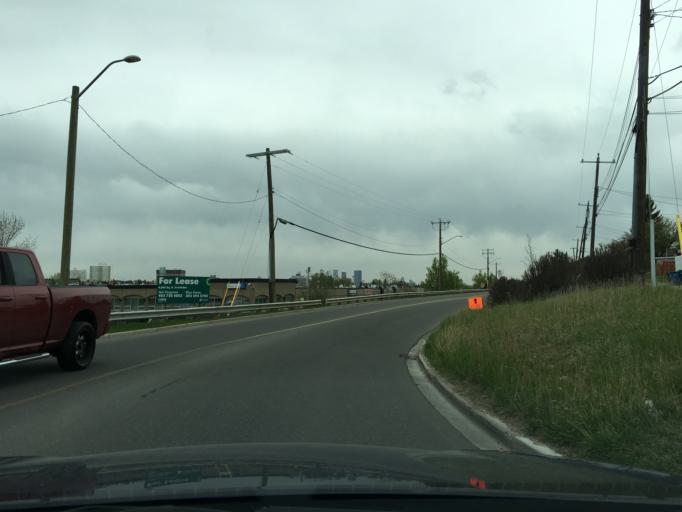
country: CA
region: Alberta
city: Calgary
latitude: 50.9820
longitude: -114.0697
